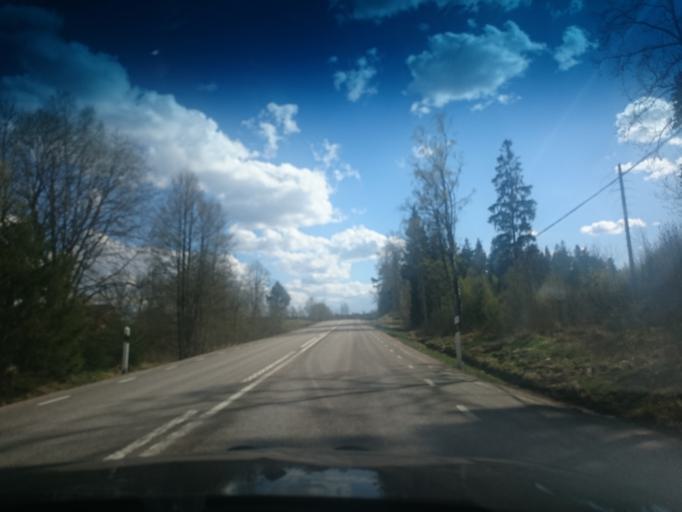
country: SE
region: Joenkoeping
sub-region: Vetlanda Kommun
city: Vetlanda
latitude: 57.2770
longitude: 15.1285
